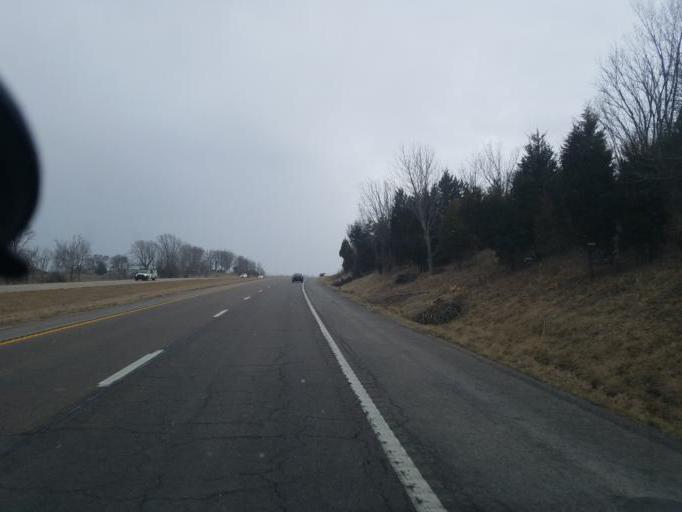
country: US
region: Missouri
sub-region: Boone County
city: Hallsville
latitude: 39.1192
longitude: -92.3303
